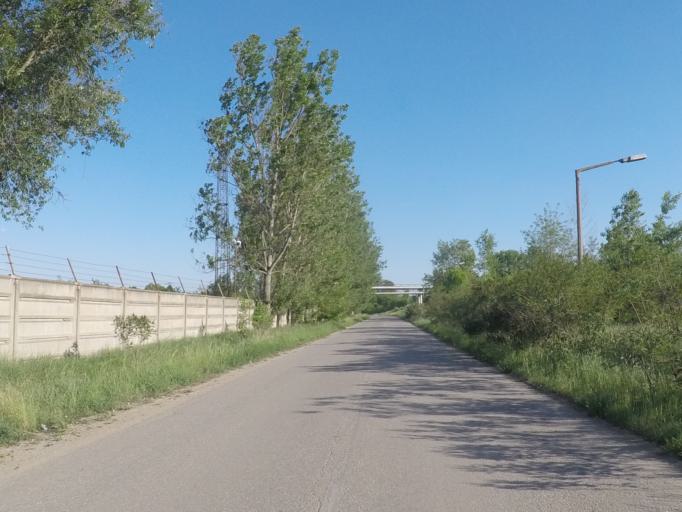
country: HU
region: Borsod-Abauj-Zemplen
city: Mucsony
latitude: 48.2367
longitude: 20.6791
